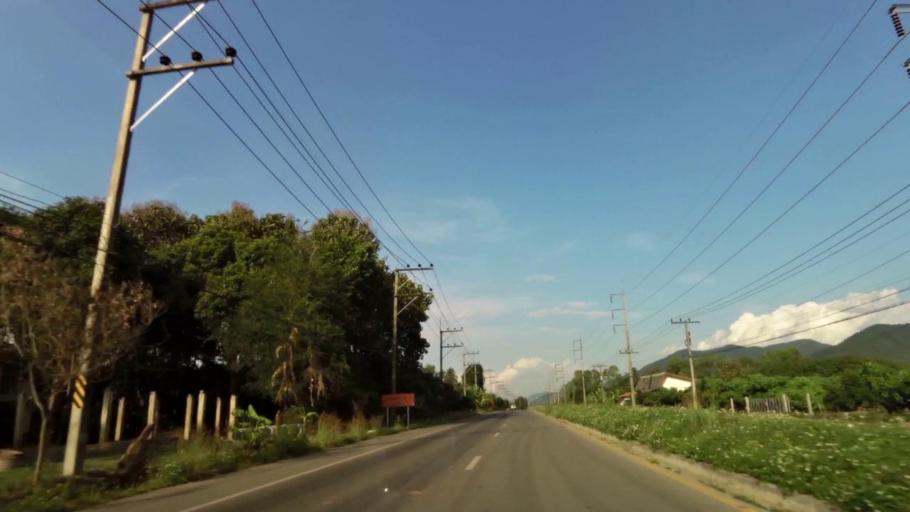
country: TH
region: Chiang Rai
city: Khun Tan
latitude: 19.8751
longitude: 100.2878
